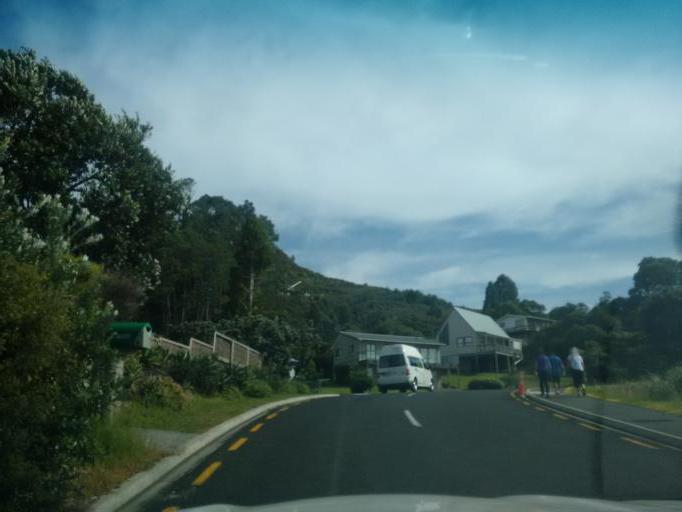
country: NZ
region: Waikato
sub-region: Thames-Coromandel District
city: Whitianga
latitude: -36.8367
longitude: 175.7992
